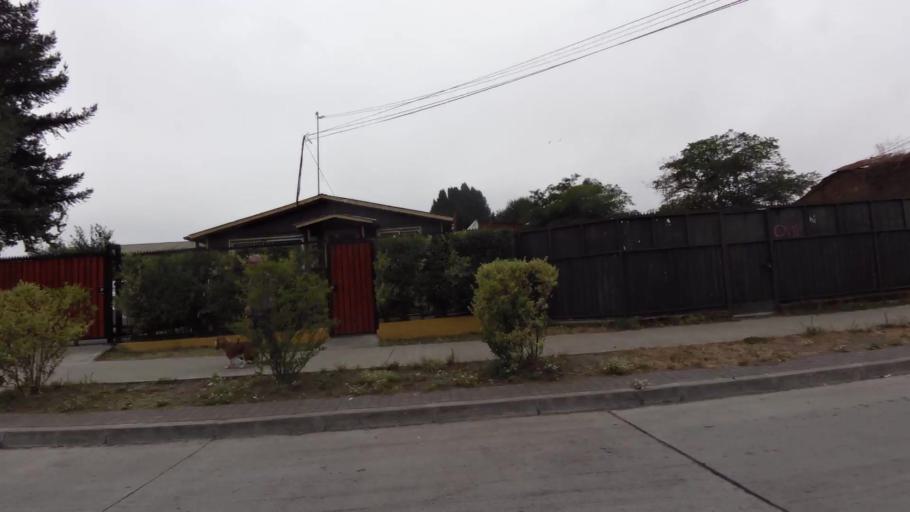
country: CL
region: Biobio
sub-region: Provincia de Concepcion
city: Concepcion
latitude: -36.8127
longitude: -73.0317
